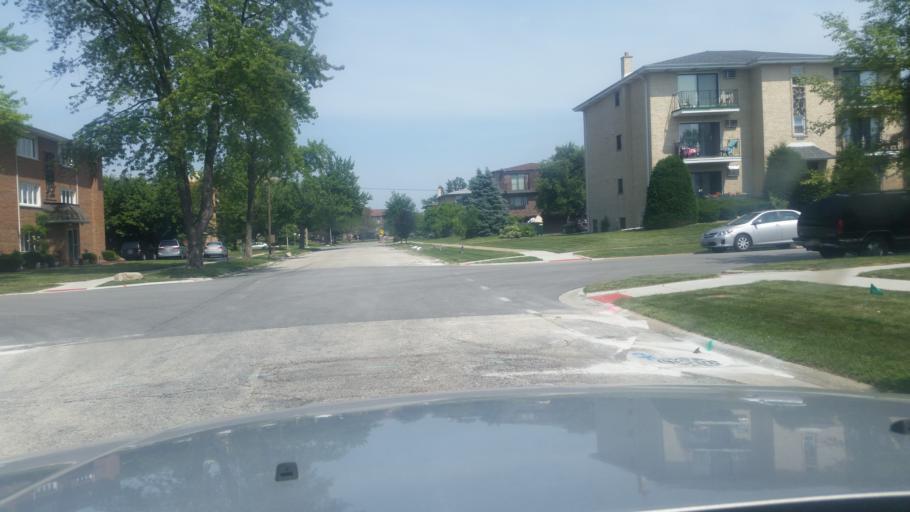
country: US
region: Illinois
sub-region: Cook County
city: Oak Lawn
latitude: 41.7032
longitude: -87.7673
